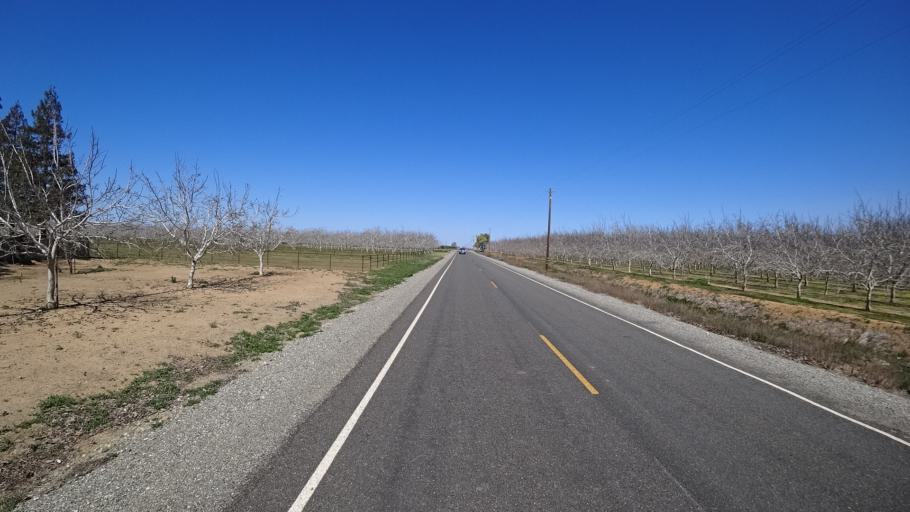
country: US
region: California
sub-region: Glenn County
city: Willows
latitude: 39.4489
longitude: -122.2488
